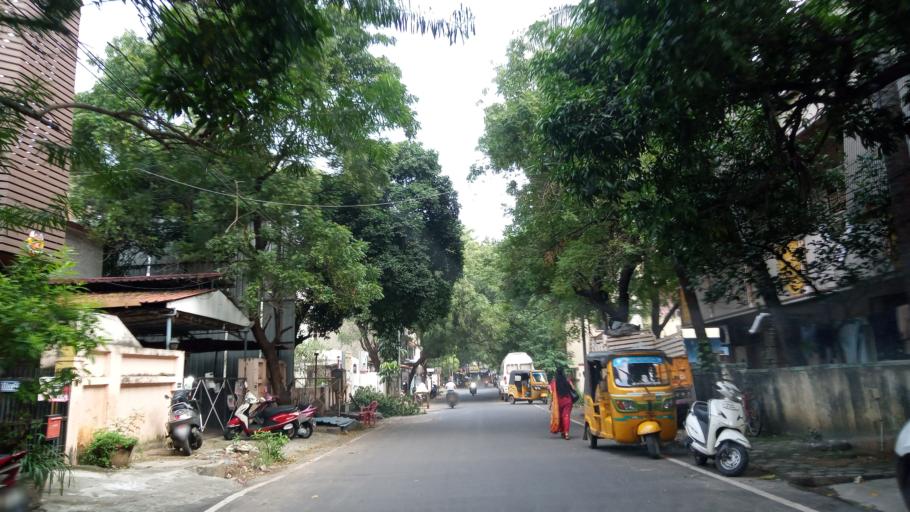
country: IN
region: Tamil Nadu
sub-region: Chennai
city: Chetput
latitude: 13.0385
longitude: 80.2193
